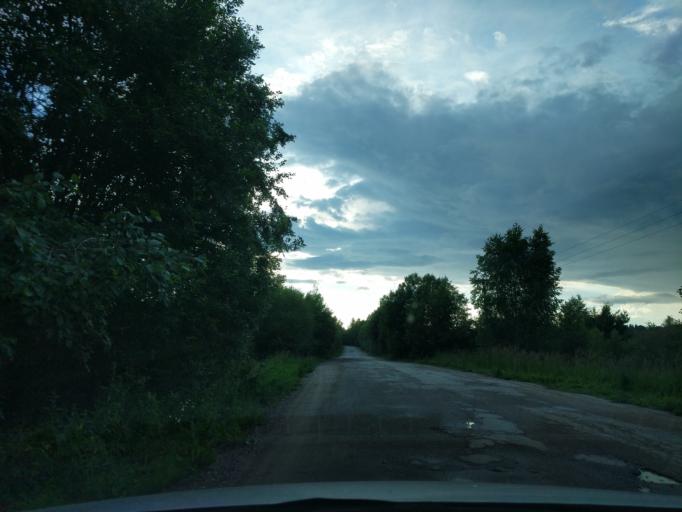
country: RU
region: Kaluga
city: Myatlevo
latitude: 54.8512
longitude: 35.5997
